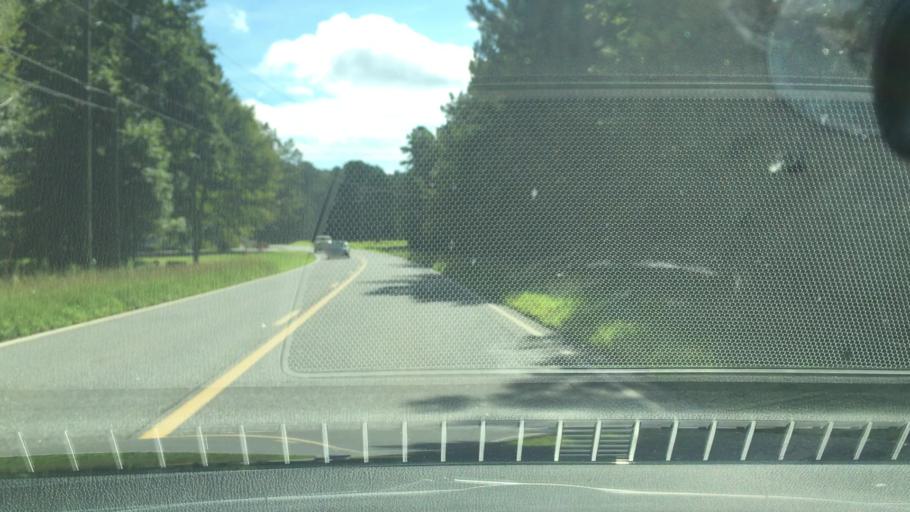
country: US
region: Georgia
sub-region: Putnam County
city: Jefferson
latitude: 33.4494
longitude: -83.3106
